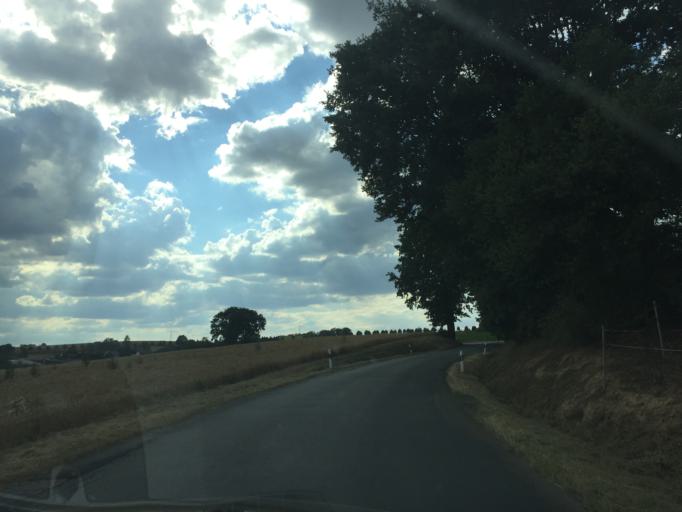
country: DE
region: Thuringia
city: Altenburg
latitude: 50.9600
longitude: 12.4423
